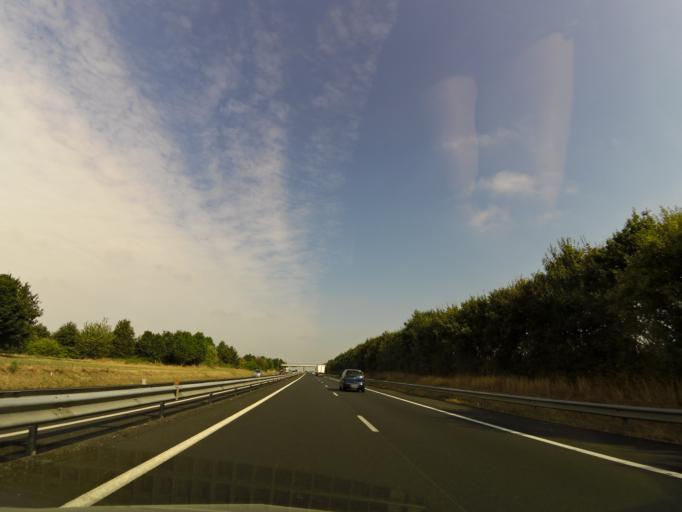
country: FR
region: Pays de la Loire
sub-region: Departement de la Vendee
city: Les Brouzils
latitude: 46.8819
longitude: -1.2894
